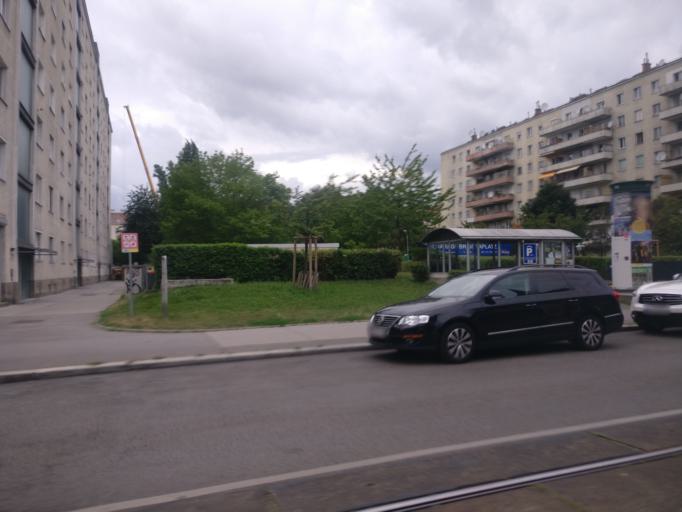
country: AT
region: Vienna
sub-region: Wien Stadt
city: Vienna
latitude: 48.2318
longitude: 16.3705
